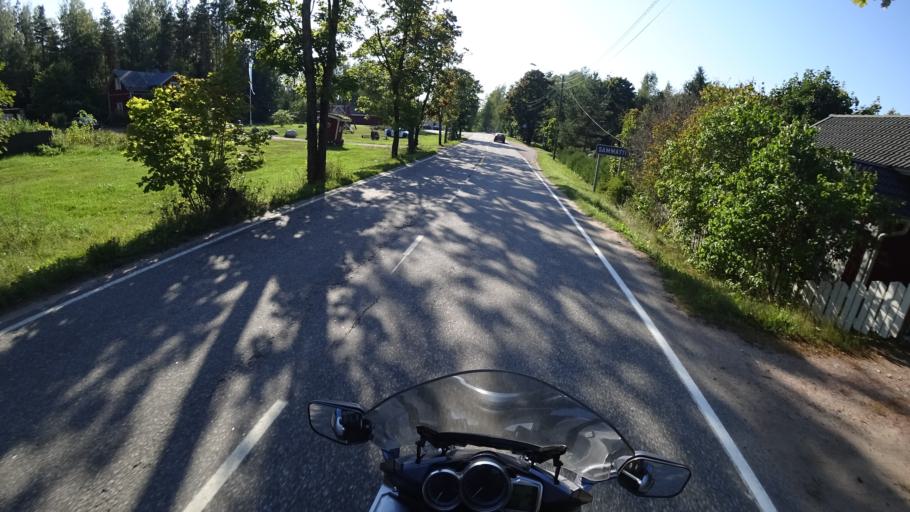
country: FI
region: Uusimaa
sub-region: Helsinki
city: Sammatti
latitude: 60.3171
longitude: 23.8341
